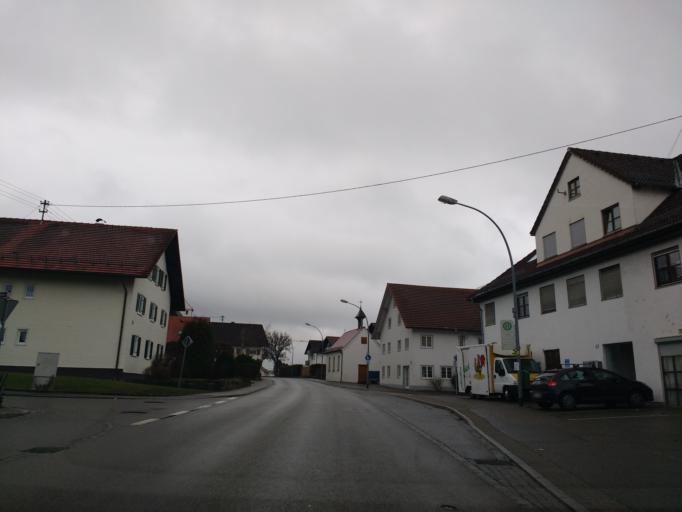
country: DE
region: Bavaria
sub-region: Swabia
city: Neuburg
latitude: 47.7665
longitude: 10.3357
